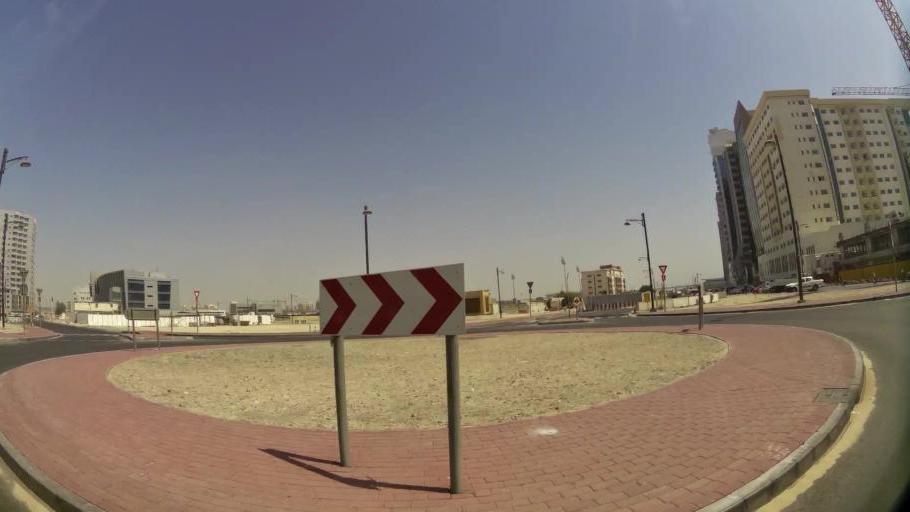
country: AE
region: Ash Shariqah
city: Sharjah
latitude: 25.2873
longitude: 55.3613
